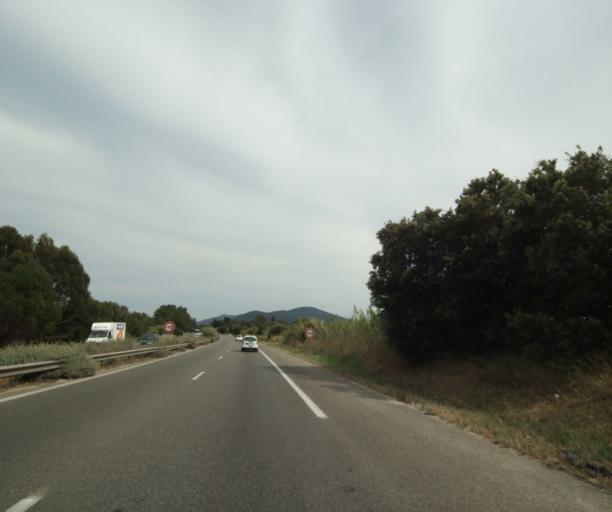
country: FR
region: Provence-Alpes-Cote d'Azur
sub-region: Departement du Var
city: La Farlede
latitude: 43.1374
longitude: 6.0418
